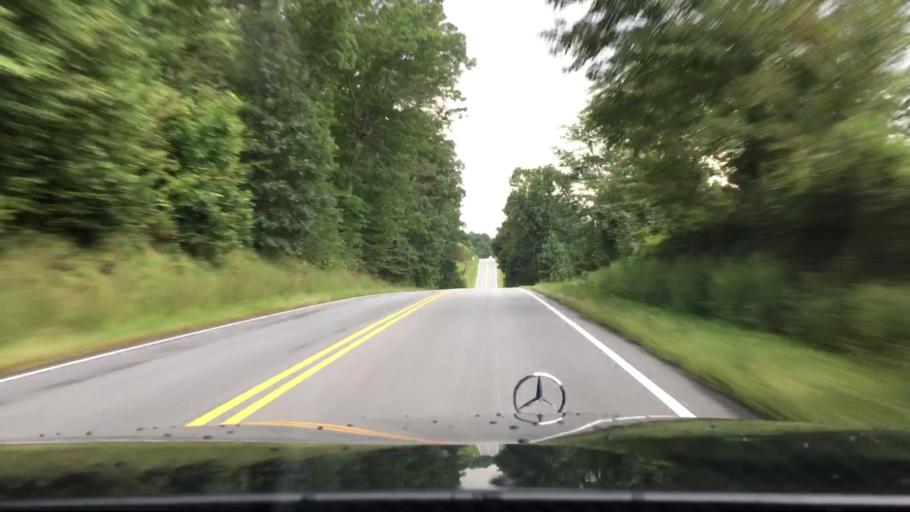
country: US
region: Virginia
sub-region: Nelson County
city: Lovingston
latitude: 37.8076
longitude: -78.9477
